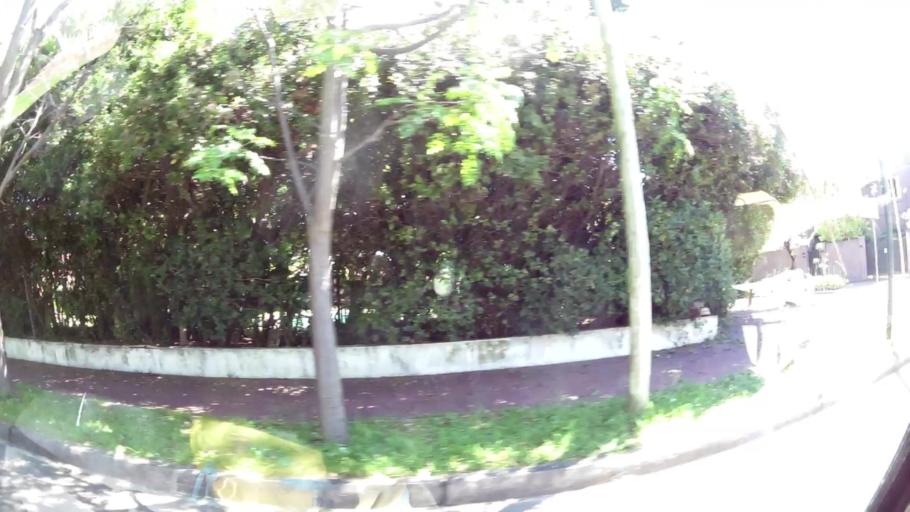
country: AR
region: Buenos Aires
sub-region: Partido de San Isidro
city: San Isidro
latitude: -34.4766
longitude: -58.5012
